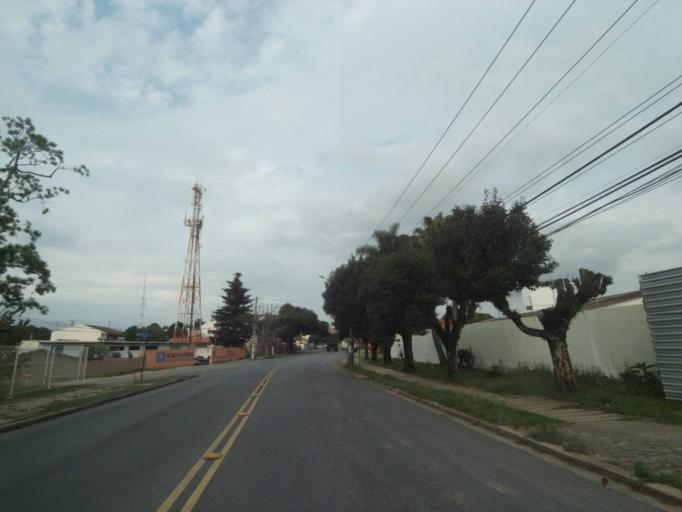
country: BR
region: Parana
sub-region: Curitiba
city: Curitiba
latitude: -25.4040
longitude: -49.2898
